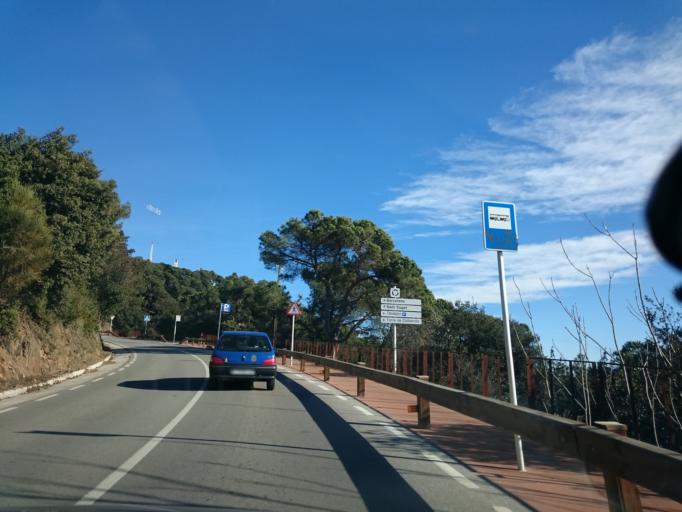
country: ES
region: Catalonia
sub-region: Provincia de Barcelona
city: Sarria-Sant Gervasi
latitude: 41.4174
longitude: 2.1163
